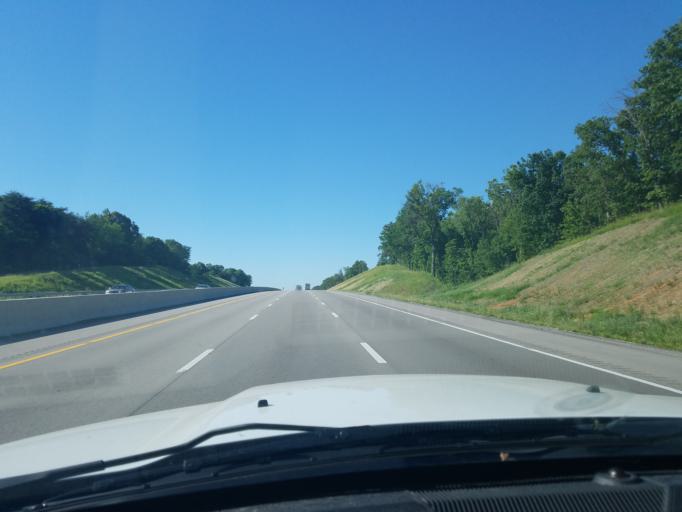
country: US
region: Kentucky
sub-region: Hart County
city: Munfordville
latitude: 37.3265
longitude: -85.9066
